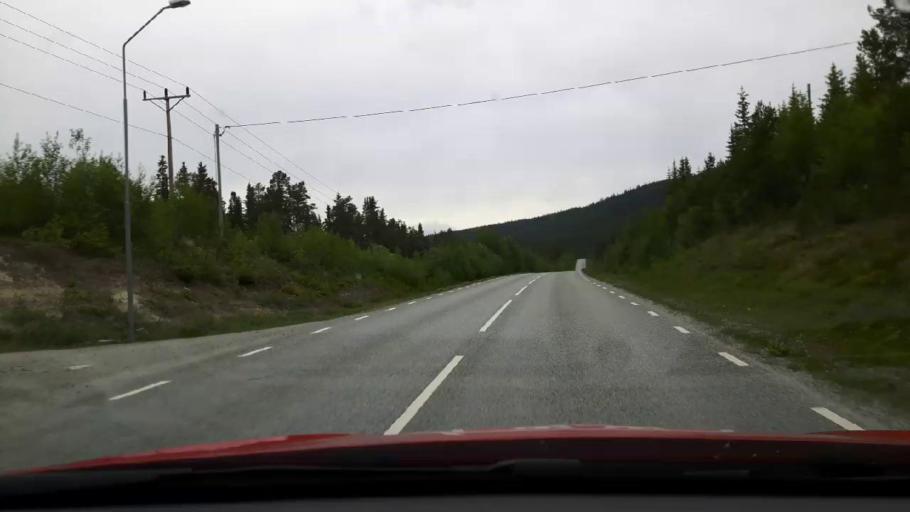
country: SE
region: Jaemtland
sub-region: Are Kommun
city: Are
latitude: 62.5745
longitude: 12.5598
